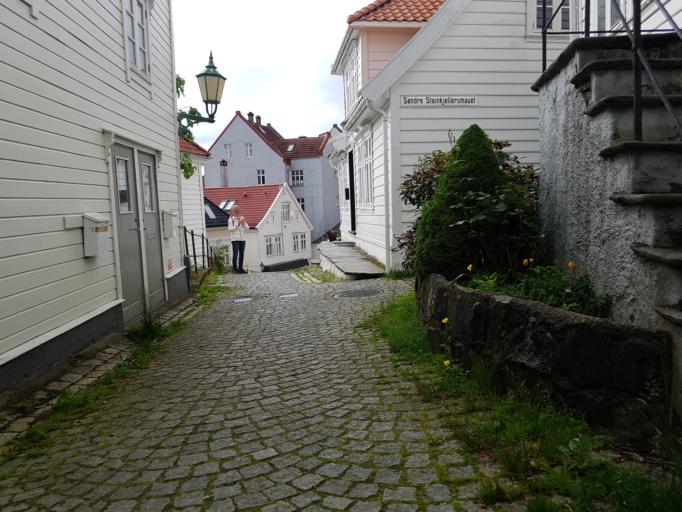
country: NO
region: Hordaland
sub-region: Bergen
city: Bergen
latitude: 60.3982
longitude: 5.3273
